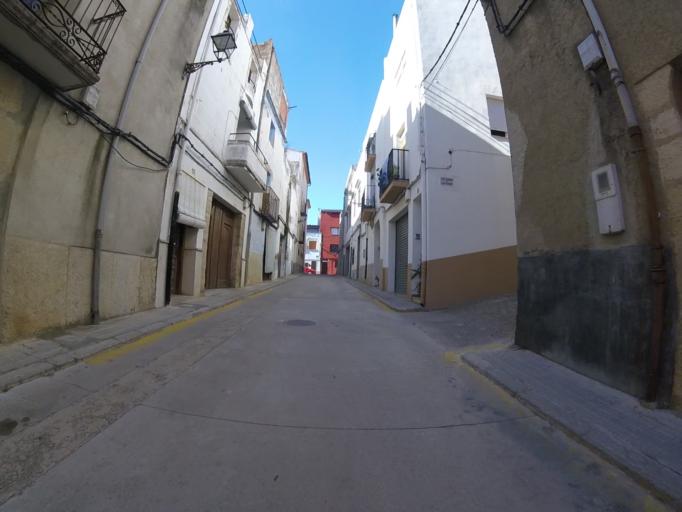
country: ES
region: Valencia
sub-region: Provincia de Castello
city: Chert/Xert
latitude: 40.4655
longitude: 0.1766
